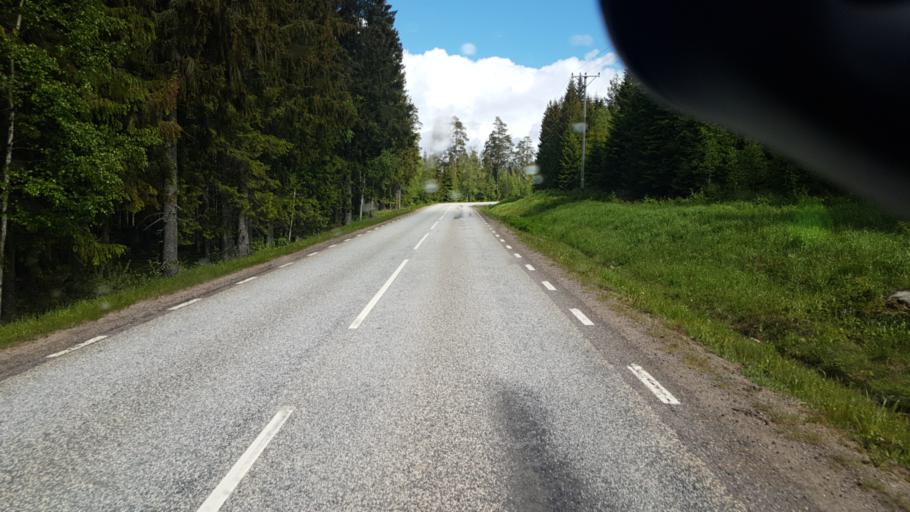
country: SE
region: Vaermland
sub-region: Arjangs Kommun
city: Arjaeng
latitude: 59.5720
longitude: 12.2082
